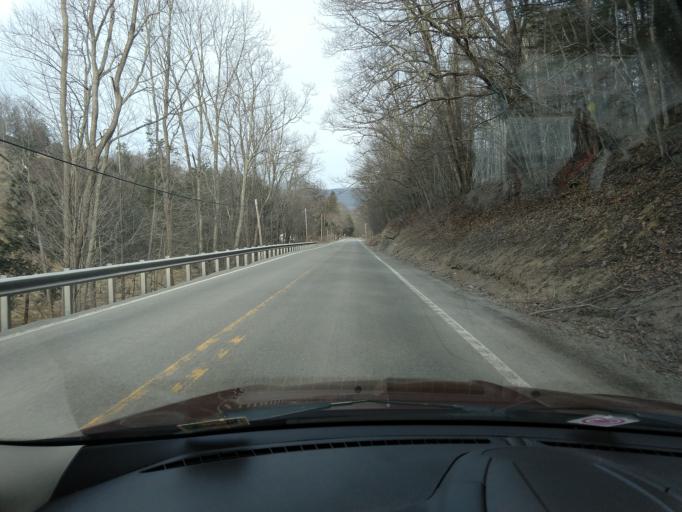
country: US
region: West Virginia
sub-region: Tucker County
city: Parsons
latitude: 38.9009
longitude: -79.4847
